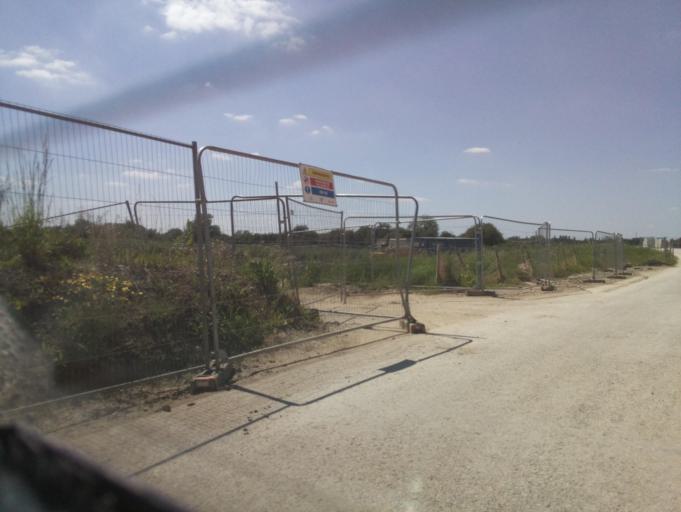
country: GB
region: England
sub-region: Borough of Swindon
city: Wroughton
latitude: 51.5429
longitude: -1.8090
